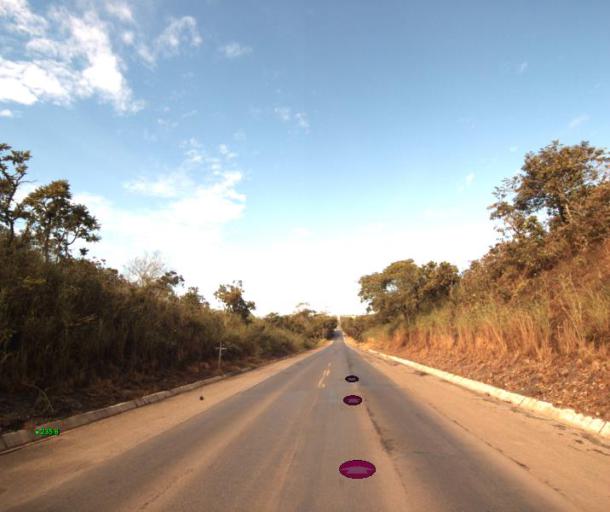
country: BR
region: Goias
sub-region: Itapaci
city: Itapaci
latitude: -14.8099
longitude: -49.2909
